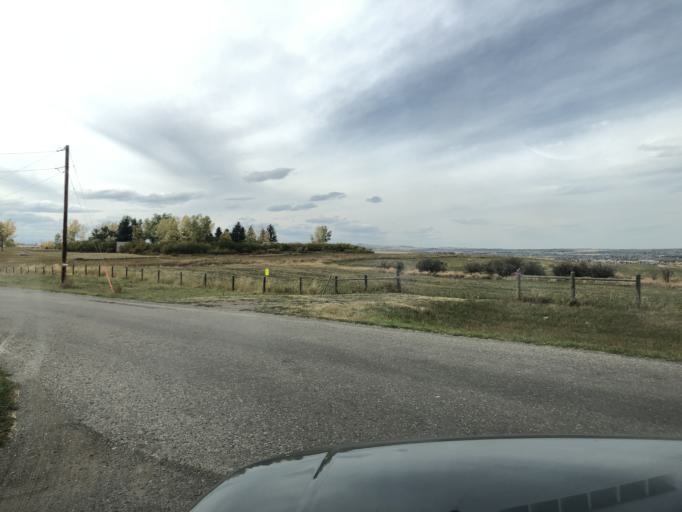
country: CA
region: Alberta
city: Okotoks
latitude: 50.6884
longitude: -113.9616
